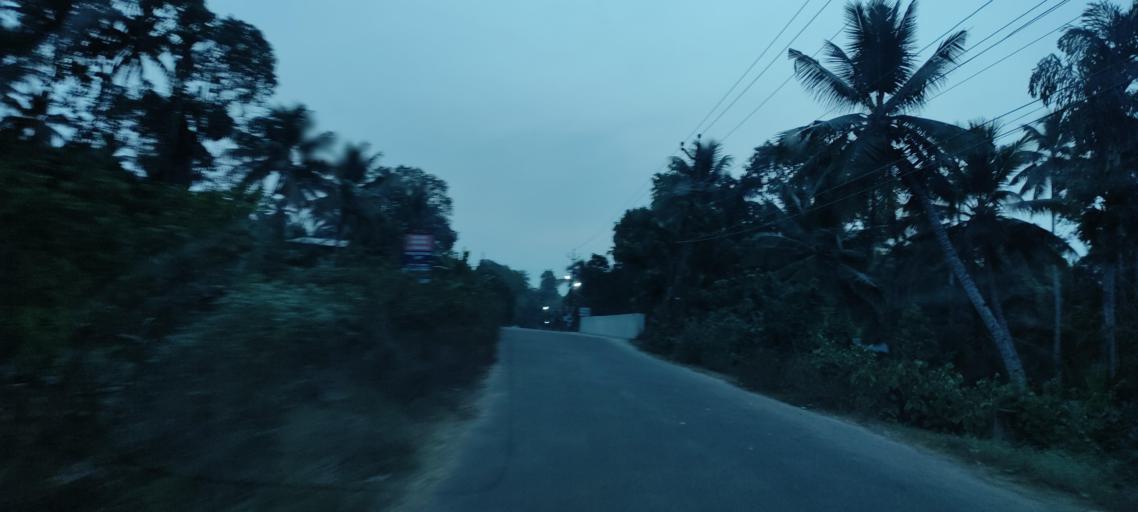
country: IN
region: Kerala
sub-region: Alappuzha
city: Mavelikara
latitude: 9.3311
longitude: 76.4747
